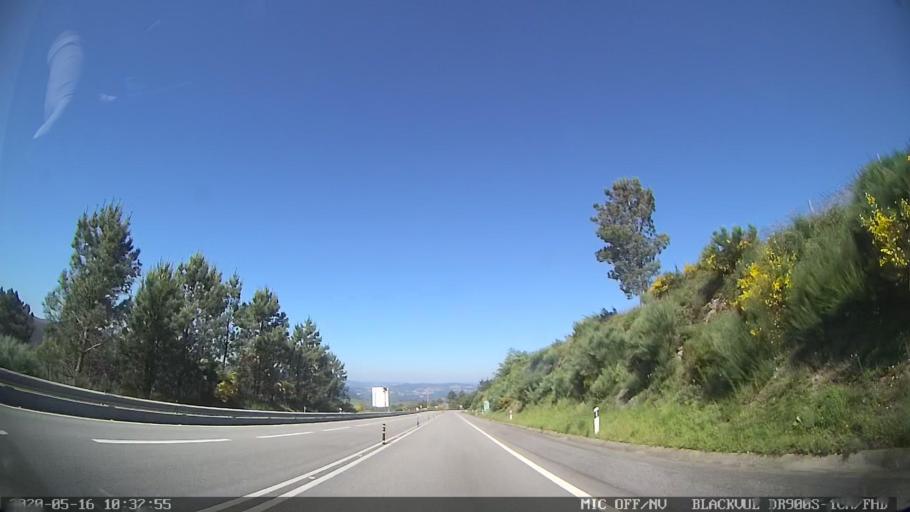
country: PT
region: Porto
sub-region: Baiao
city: Valadares
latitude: 41.2560
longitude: -7.9644
